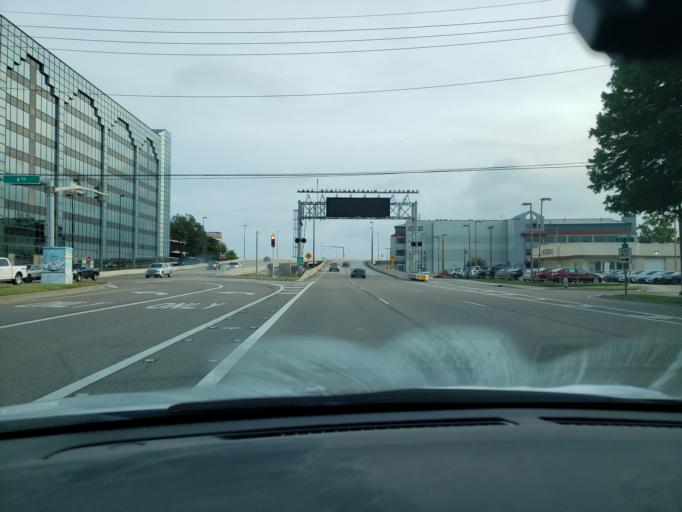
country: US
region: Louisiana
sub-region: Jefferson Parish
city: Metairie
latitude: 30.0174
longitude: -90.1545
